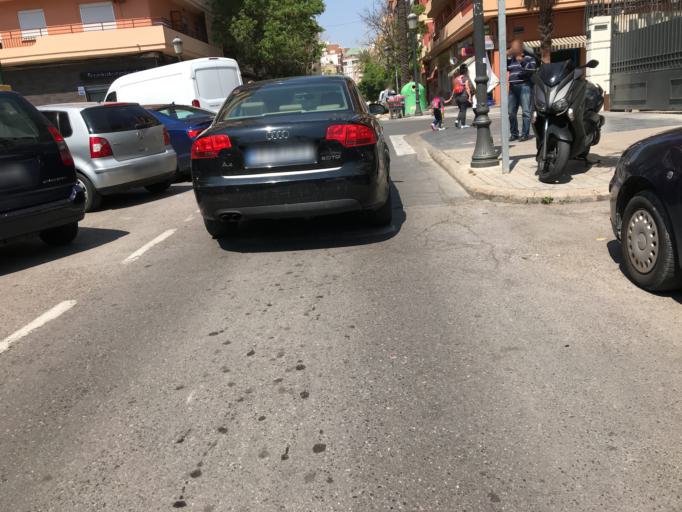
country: ES
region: Valencia
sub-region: Provincia de Valencia
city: Valencia
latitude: 39.4695
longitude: -0.3513
